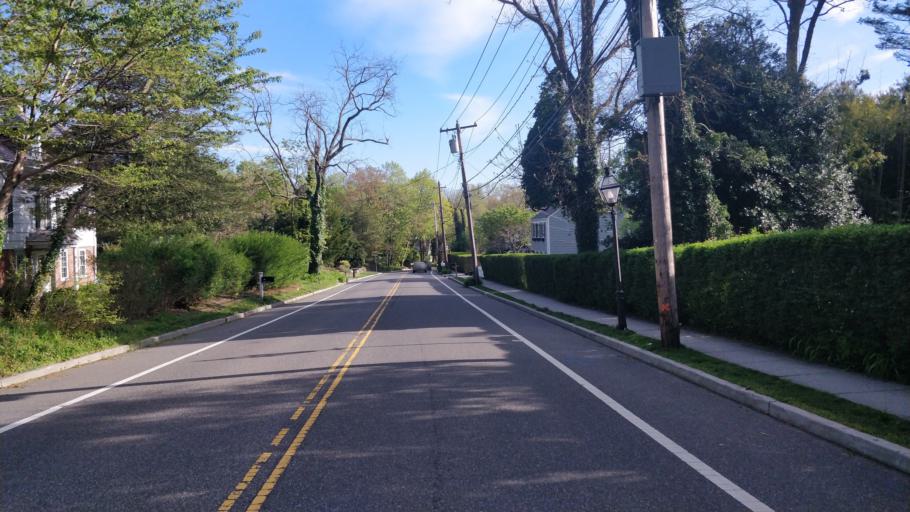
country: US
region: New York
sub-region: Suffolk County
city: Stony Brook
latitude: 40.9222
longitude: -73.1453
